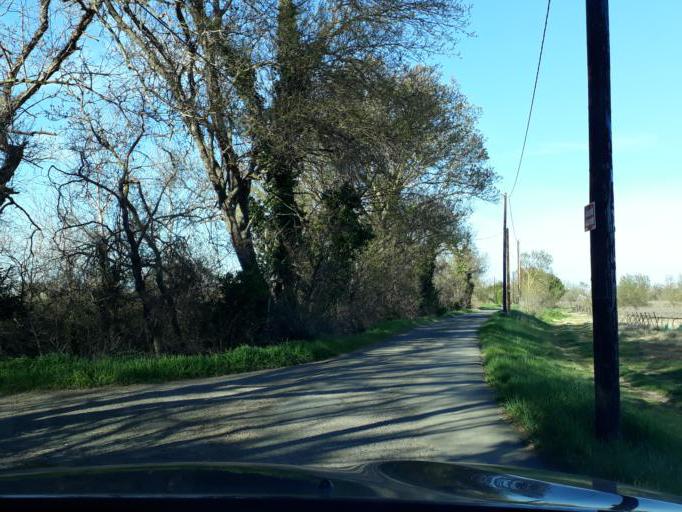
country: FR
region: Languedoc-Roussillon
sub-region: Departement de l'Herault
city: Agde
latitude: 43.3277
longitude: 3.4516
